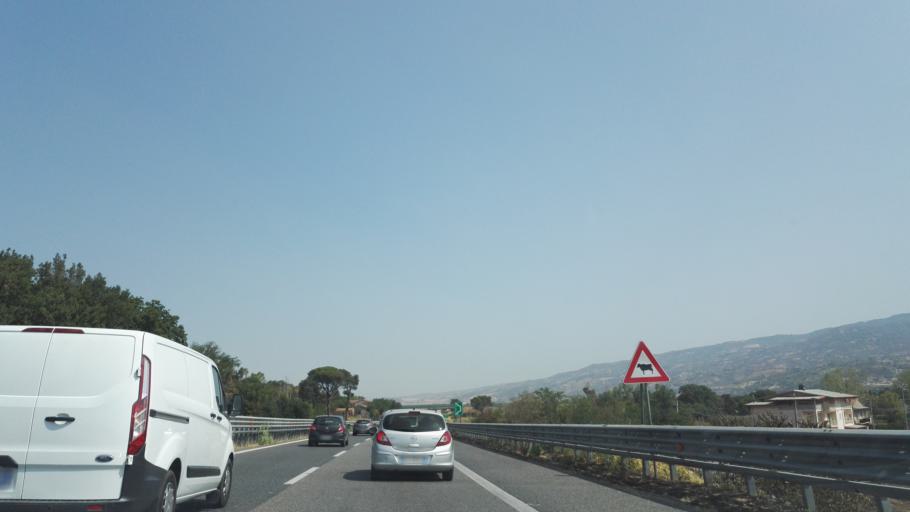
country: IT
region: Calabria
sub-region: Provincia di Cosenza
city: Quattromiglia
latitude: 39.3610
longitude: 16.2340
